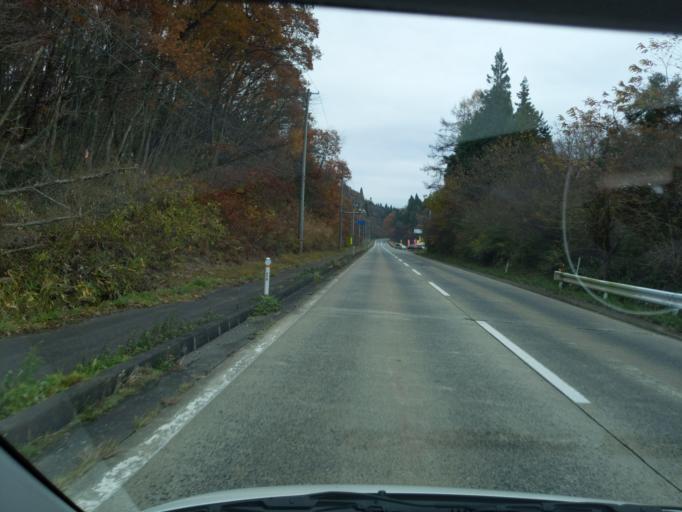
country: JP
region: Iwate
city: Kitakami
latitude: 39.3002
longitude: 141.2046
